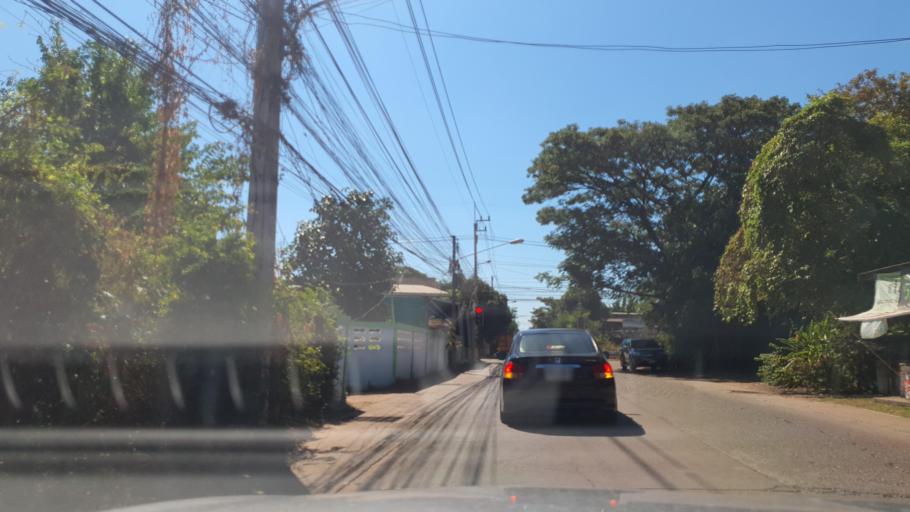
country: TH
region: Sakon Nakhon
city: Sakon Nakhon
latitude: 17.1575
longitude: 104.1213
